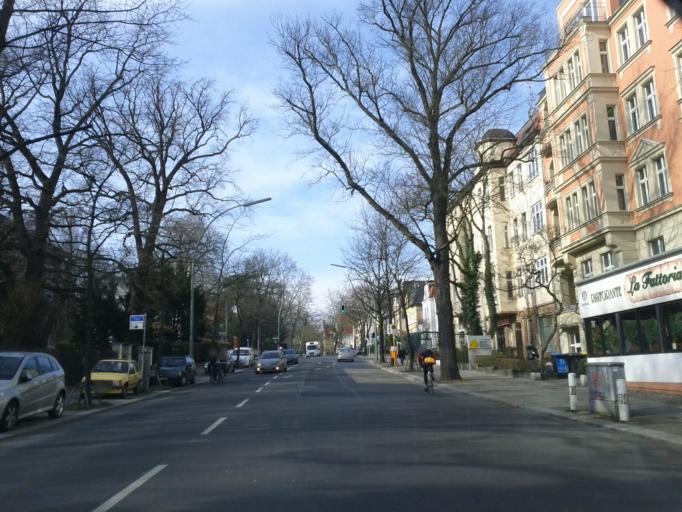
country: DE
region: Berlin
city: Steglitz Bezirk
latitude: 52.4584
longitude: 13.3165
